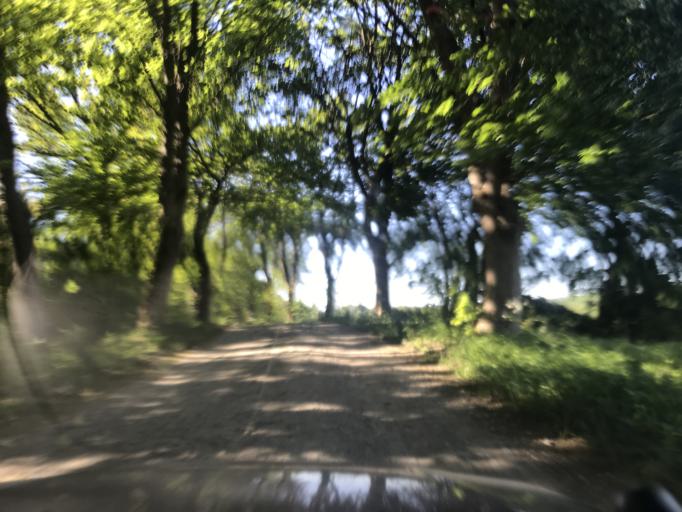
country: PL
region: West Pomeranian Voivodeship
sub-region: Powiat swidwinski
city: Polczyn-Zdroj
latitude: 53.7166
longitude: 16.1110
